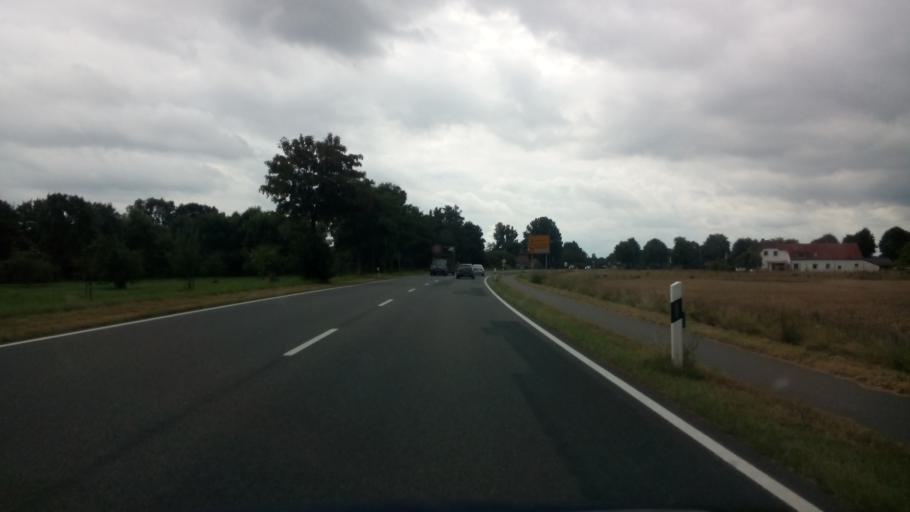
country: DE
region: Lower Saxony
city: Huede
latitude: 52.5109
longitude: 8.3763
